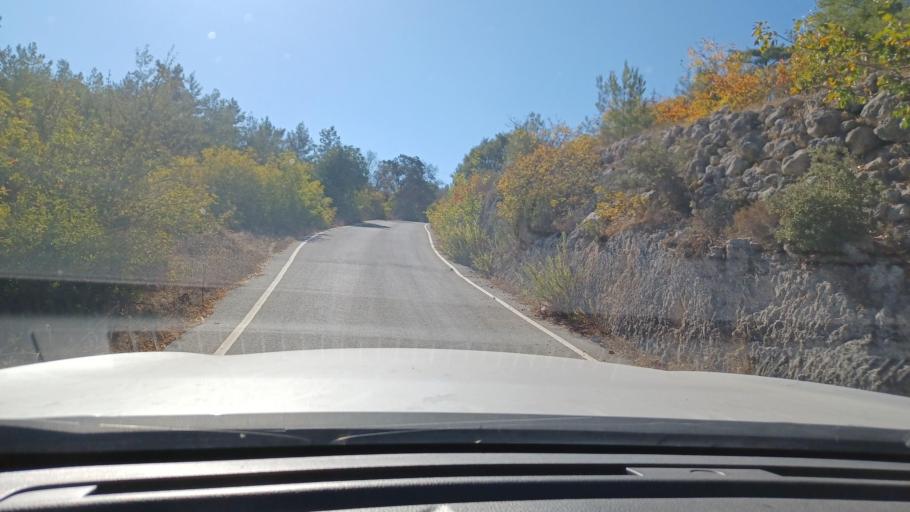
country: CY
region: Pafos
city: Polis
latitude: 34.9936
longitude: 32.5157
